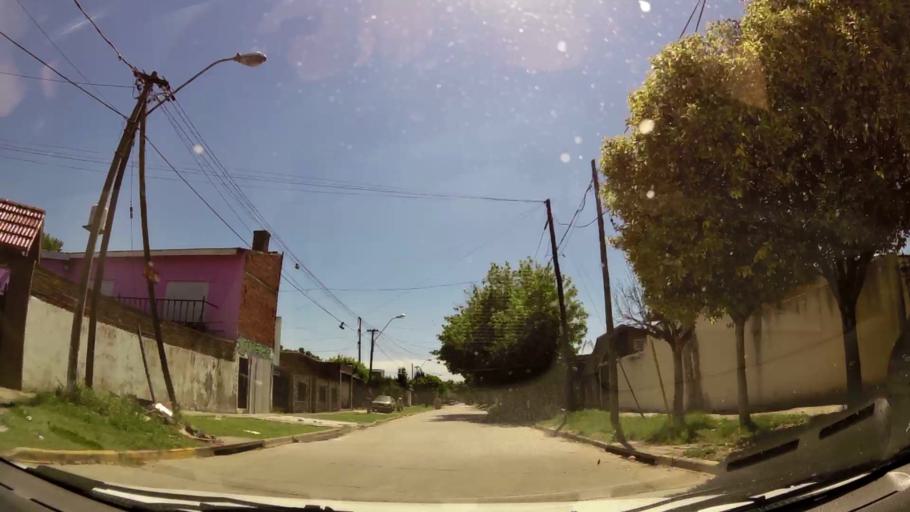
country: AR
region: Buenos Aires
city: Ituzaingo
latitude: -34.6788
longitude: -58.6757
